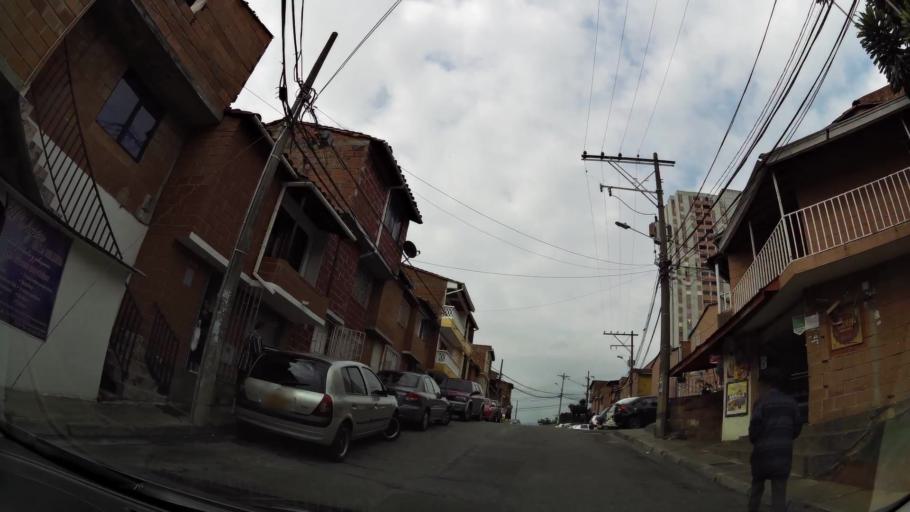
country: CO
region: Antioquia
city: Medellin
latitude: 6.2802
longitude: -75.5988
